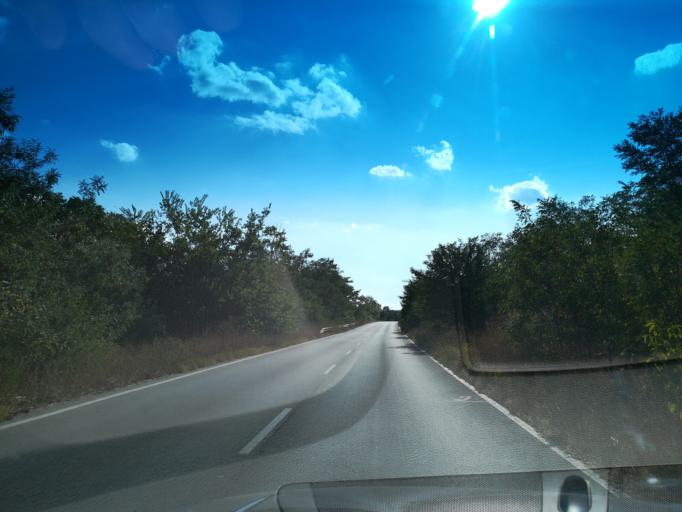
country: BG
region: Khaskovo
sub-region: Obshtina Mineralni Bani
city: Mineralni Bani
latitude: 42.0160
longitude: 25.4066
